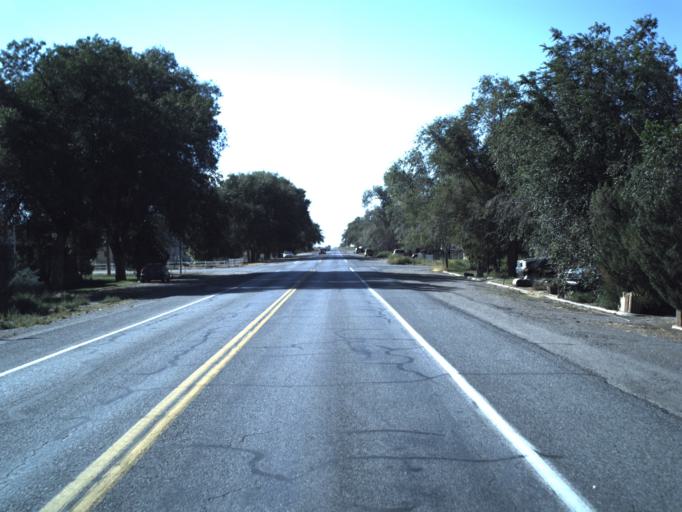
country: US
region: Utah
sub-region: Millard County
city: Delta
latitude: 39.2877
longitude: -112.6528
